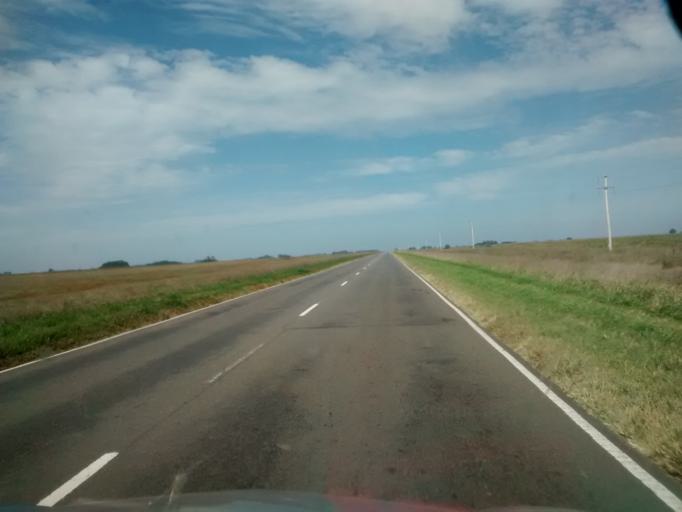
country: AR
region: Buenos Aires
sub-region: Partido de Ayacucho
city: Ayacucho
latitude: -36.9964
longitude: -58.5357
